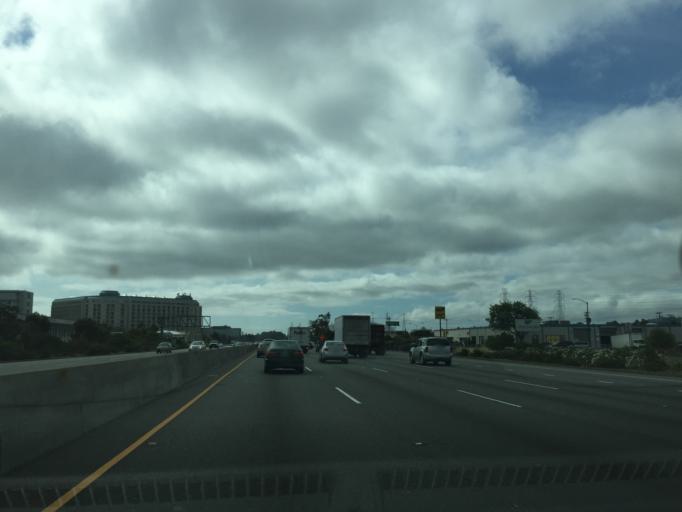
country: US
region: California
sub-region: San Mateo County
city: Burlingame
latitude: 37.5959
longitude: -122.3703
